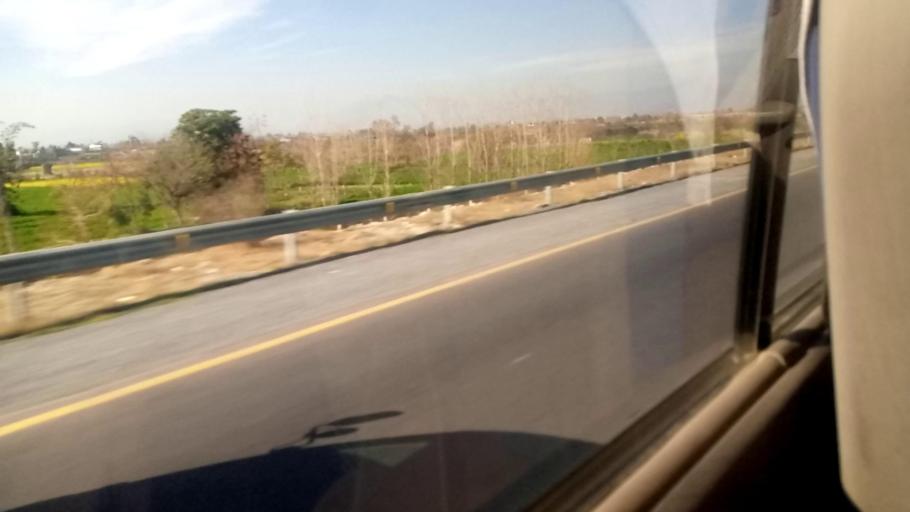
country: PK
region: Khyber Pakhtunkhwa
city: Mardan
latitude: 34.4084
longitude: 72.1298
